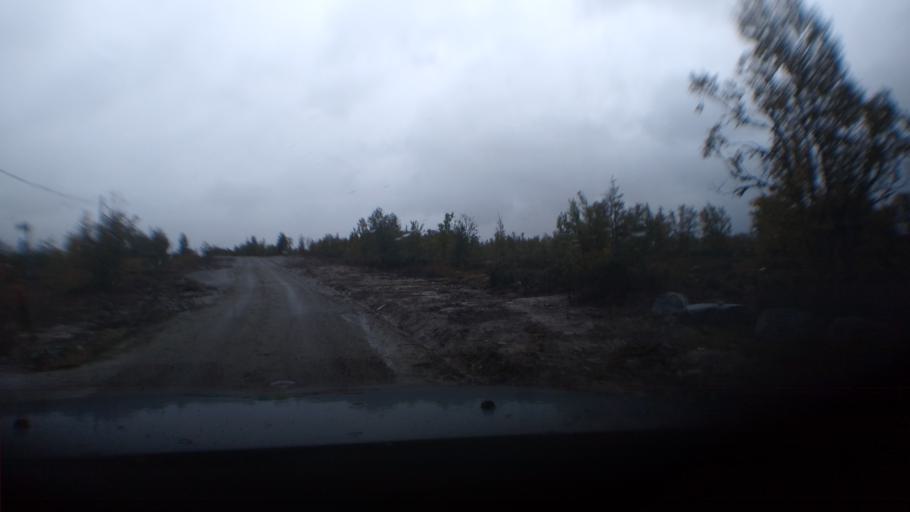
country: NO
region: Oppland
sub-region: Ringebu
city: Ringebu
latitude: 61.6591
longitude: 10.1038
